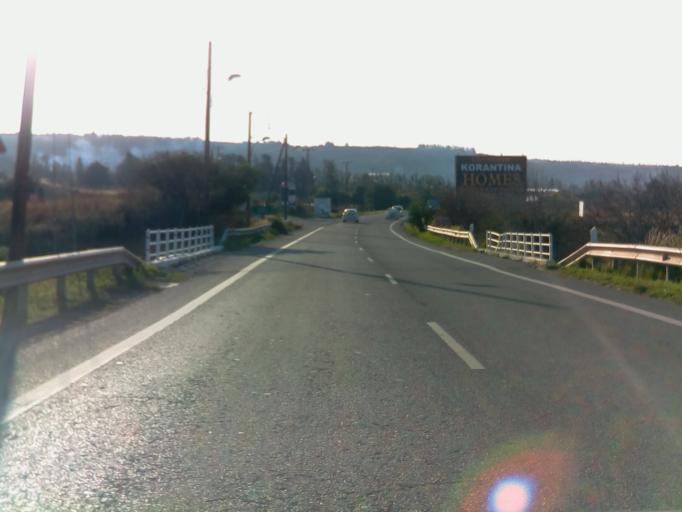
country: CY
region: Pafos
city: Pegeia
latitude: 34.8518
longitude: 32.3828
